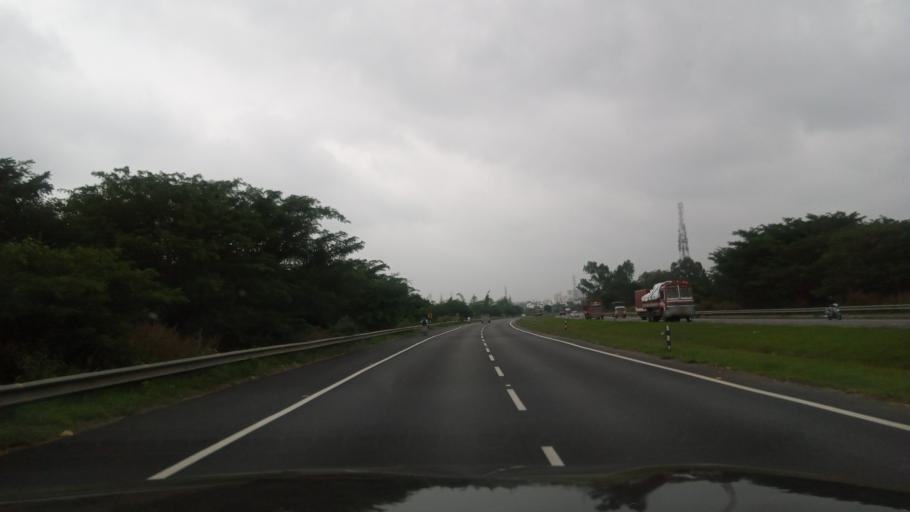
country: IN
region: Karnataka
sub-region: Bangalore Urban
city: Bangalore
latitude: 12.8664
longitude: 77.6302
